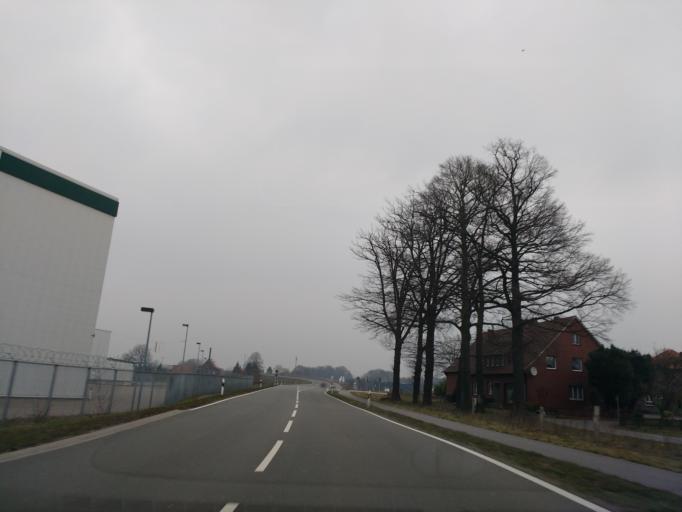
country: DE
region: North Rhine-Westphalia
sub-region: Regierungsbezirk Munster
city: Lotte
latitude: 52.2872
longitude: 7.9281
